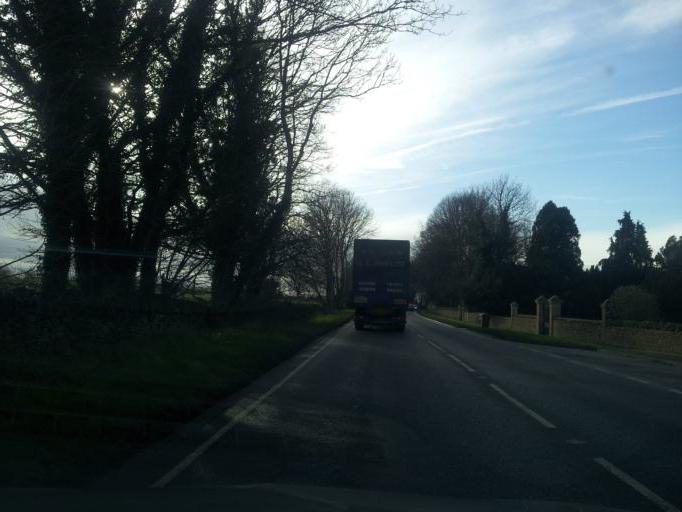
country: GB
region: England
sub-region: District of Rutland
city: Ketton
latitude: 52.6119
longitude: -0.5316
